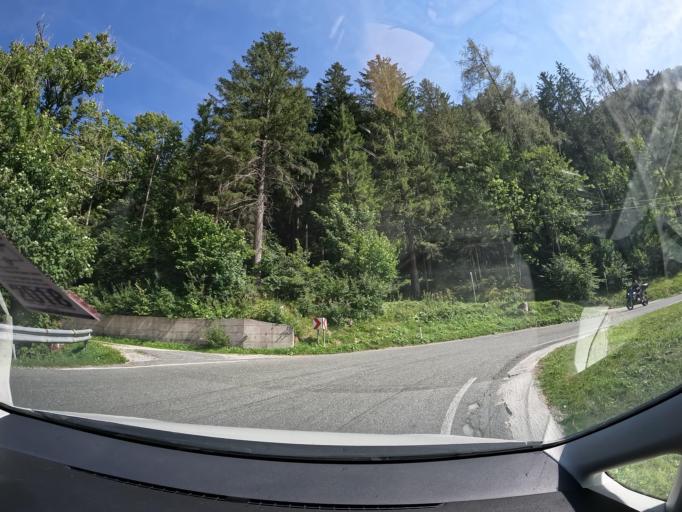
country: AT
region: Carinthia
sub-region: Politischer Bezirk Klagenfurt Land
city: Ludmannsdorf
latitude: 46.5087
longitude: 14.1001
